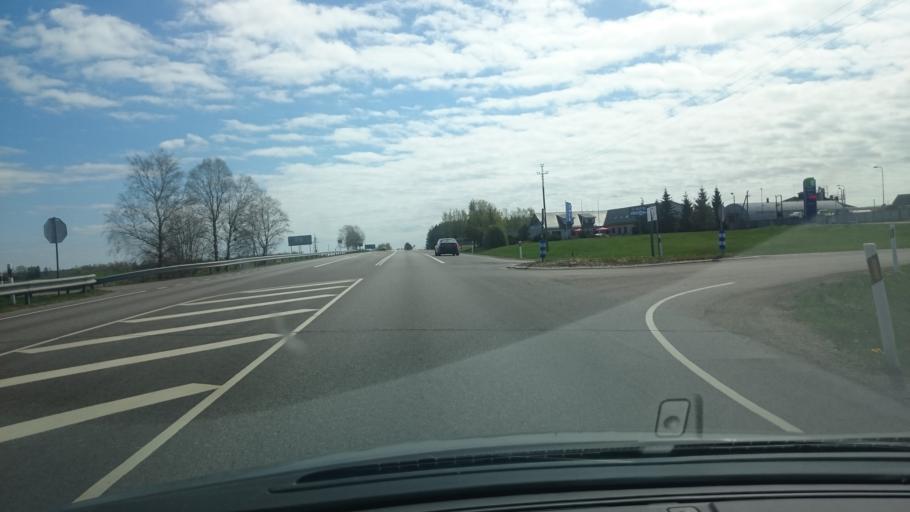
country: EE
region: Ida-Virumaa
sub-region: Kohtla-Jaerve linn
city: Kohtla-Jarve
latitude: 59.4110
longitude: 27.3087
